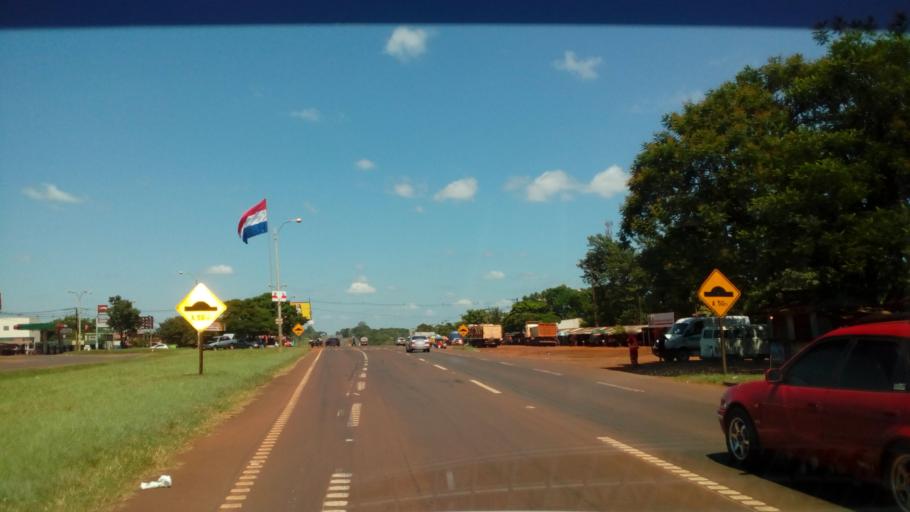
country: PY
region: Alto Parana
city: Colonia Yguazu
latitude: -25.4839
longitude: -54.8962
